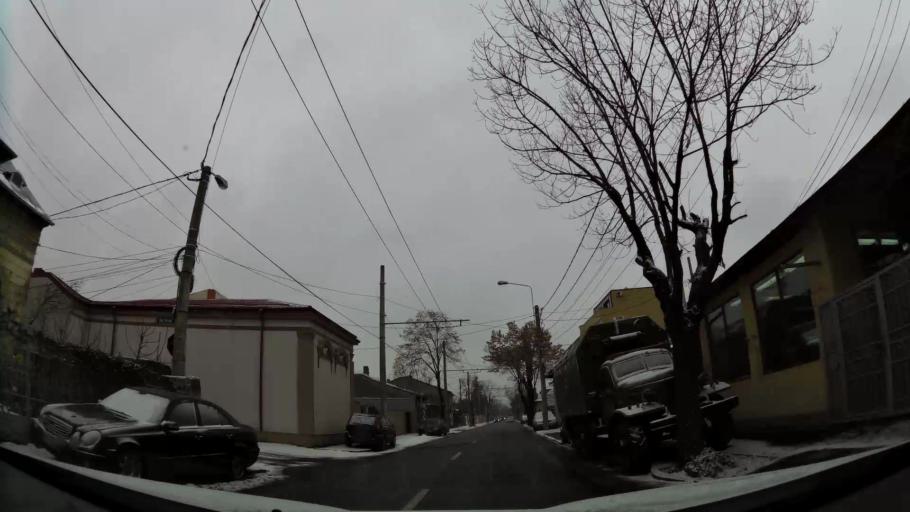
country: RO
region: Prahova
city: Ploiesti
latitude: 44.9418
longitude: 26.0134
